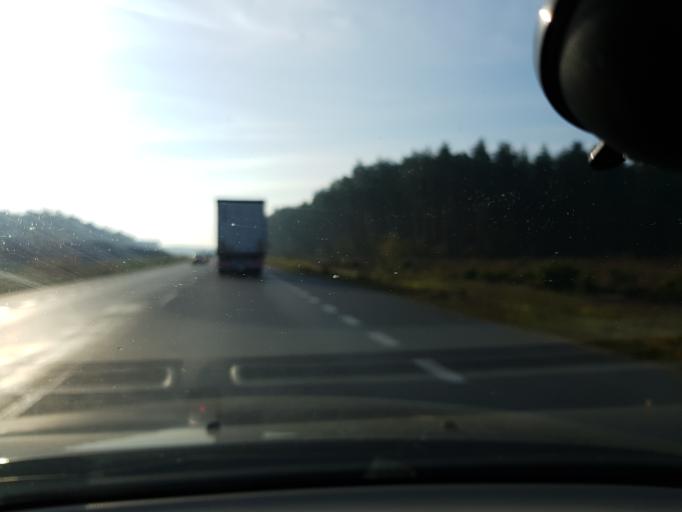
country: PL
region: Masovian Voivodeship
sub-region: Powiat otwocki
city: Otwock
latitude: 52.1575
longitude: 21.3081
